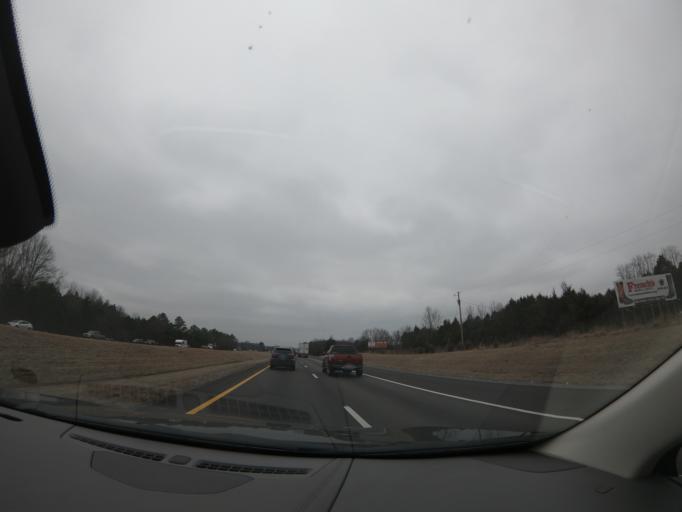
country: US
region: Tennessee
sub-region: Rutherford County
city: Plainview
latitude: 35.7655
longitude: -86.3568
